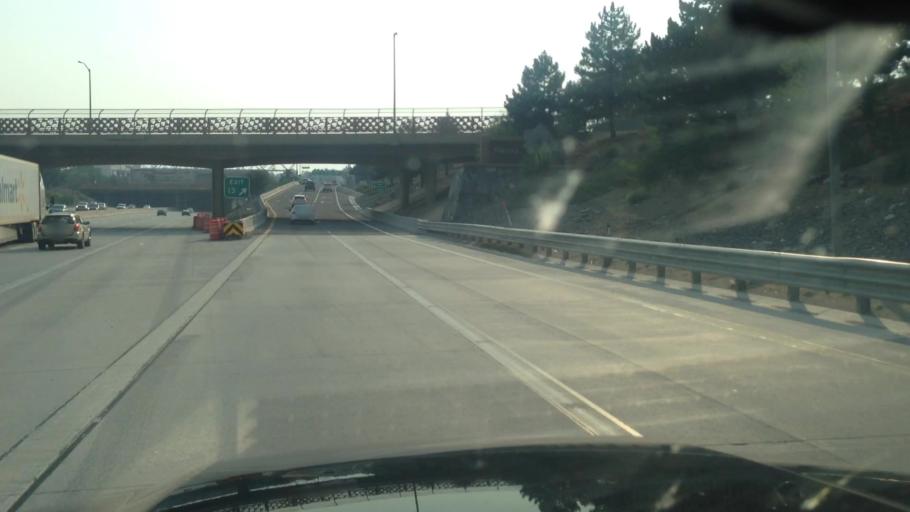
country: US
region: Nevada
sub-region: Washoe County
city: Reno
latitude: 39.5361
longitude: -119.8109
